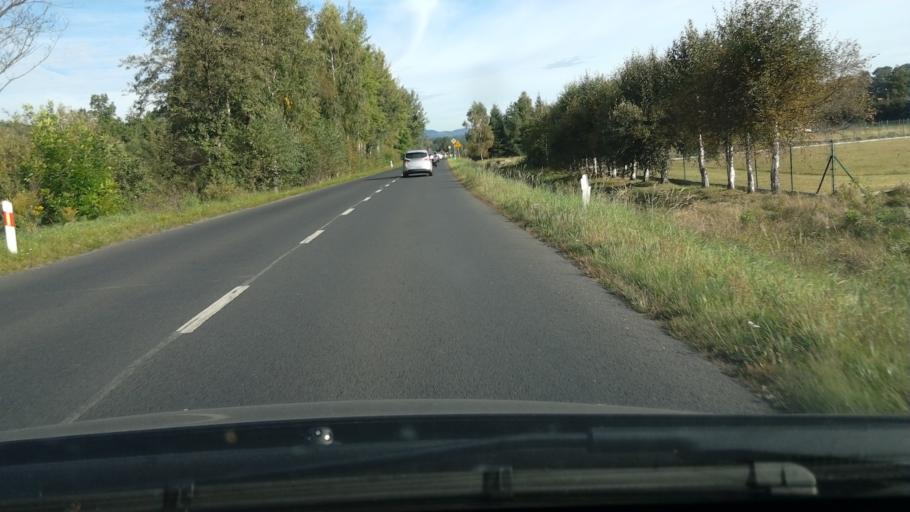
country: PL
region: Lower Silesian Voivodeship
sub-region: Powiat jeleniogorski
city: Myslakowice
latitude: 50.8357
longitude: 15.7739
